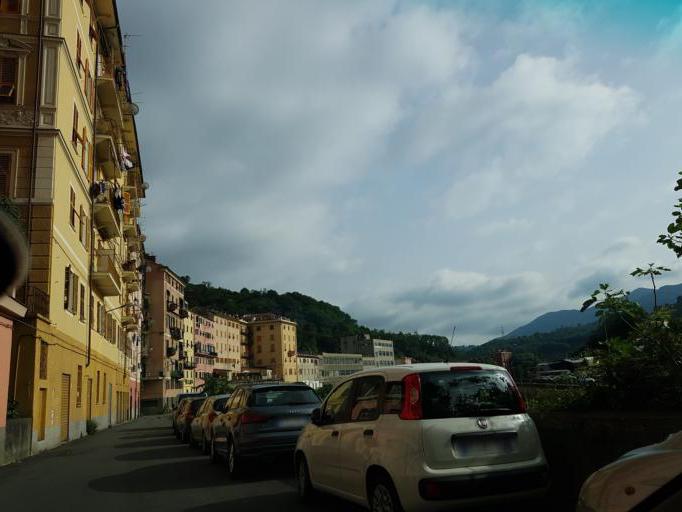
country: IT
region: Liguria
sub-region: Provincia di Genova
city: Santa Marta
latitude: 44.4942
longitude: 8.9048
